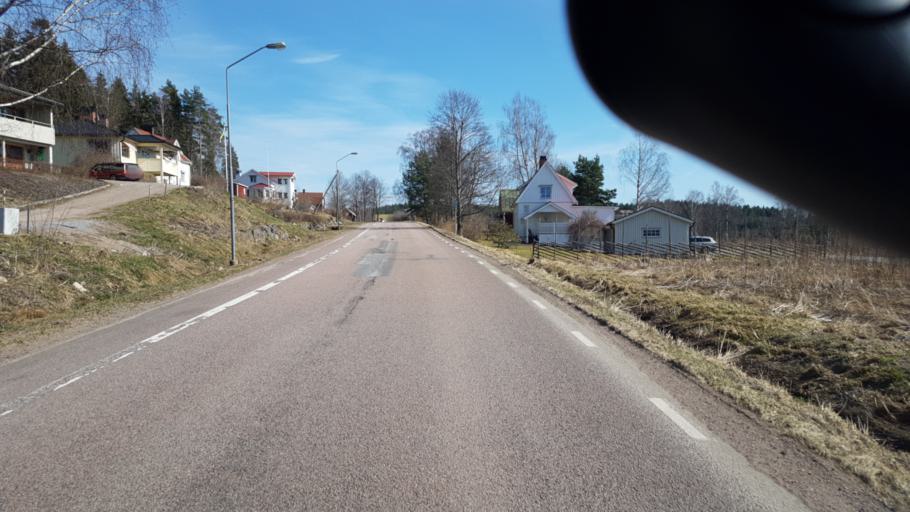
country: SE
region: Vaermland
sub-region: Arvika Kommun
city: Arvika
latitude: 59.6257
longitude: 12.8333
